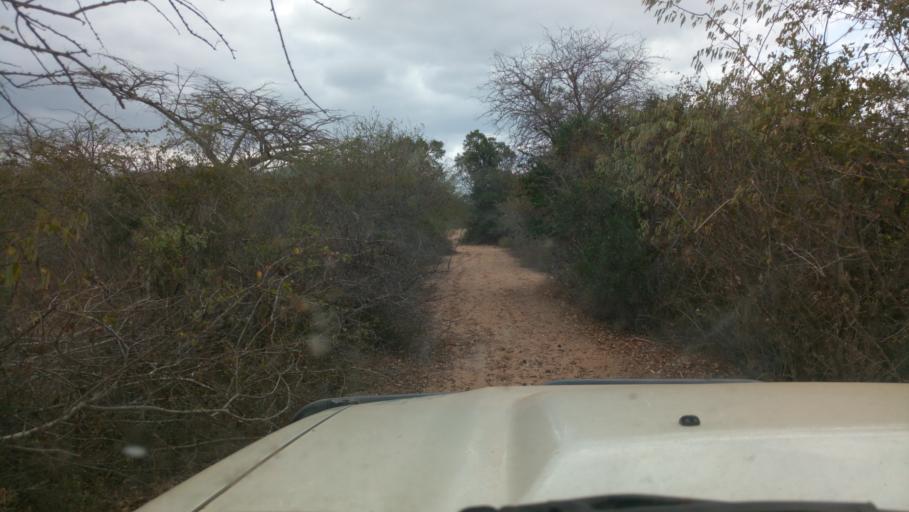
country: KE
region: Kitui
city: Kitui
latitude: -1.8507
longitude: 38.3763
